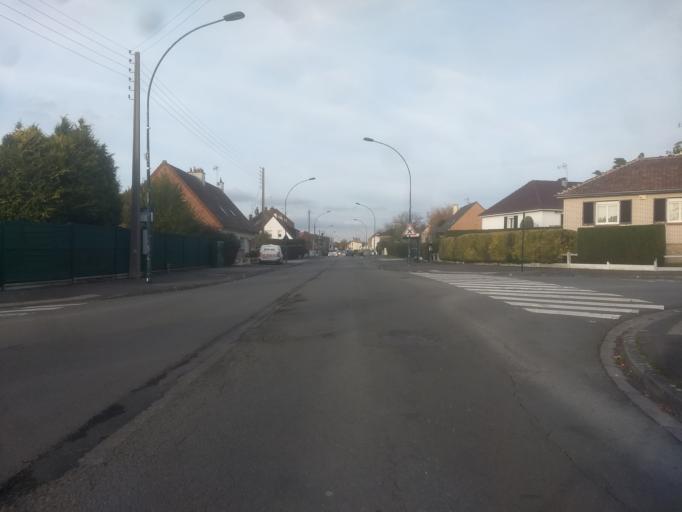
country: FR
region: Nord-Pas-de-Calais
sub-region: Departement du Pas-de-Calais
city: Achicourt
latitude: 50.2702
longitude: 2.7744
